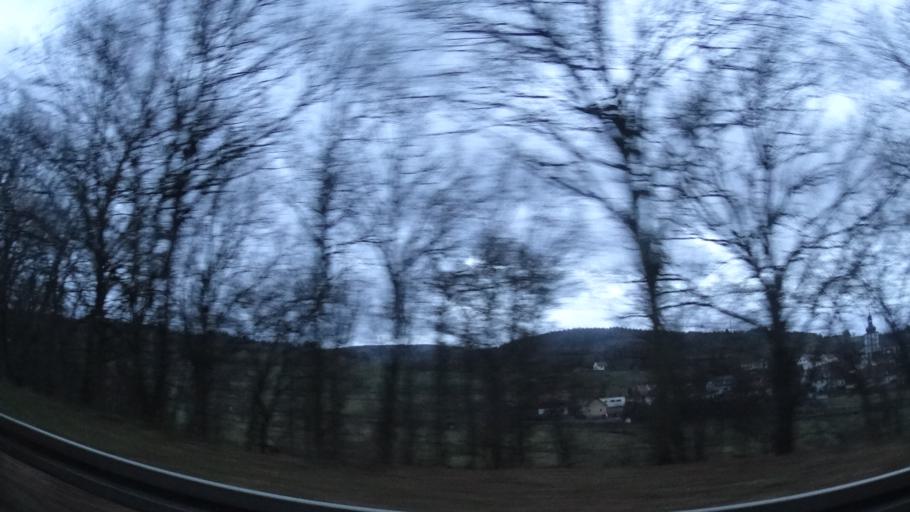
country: DE
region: Bavaria
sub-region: Regierungsbezirk Unterfranken
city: Motten
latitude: 50.4539
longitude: 9.7976
